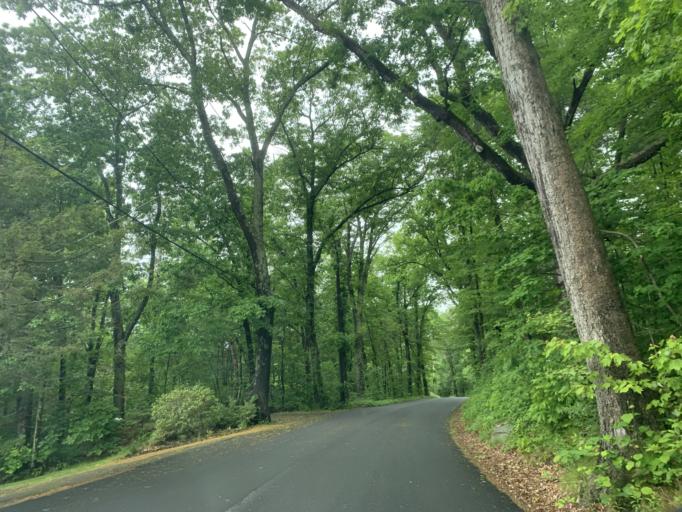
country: US
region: Massachusetts
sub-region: Worcester County
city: Upton
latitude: 42.1808
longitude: -71.6207
